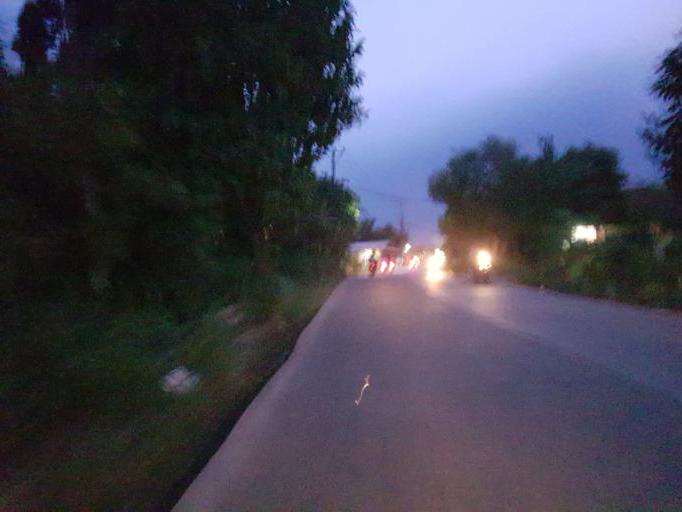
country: ID
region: West Java
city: Serpong
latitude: -6.3123
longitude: 106.6561
